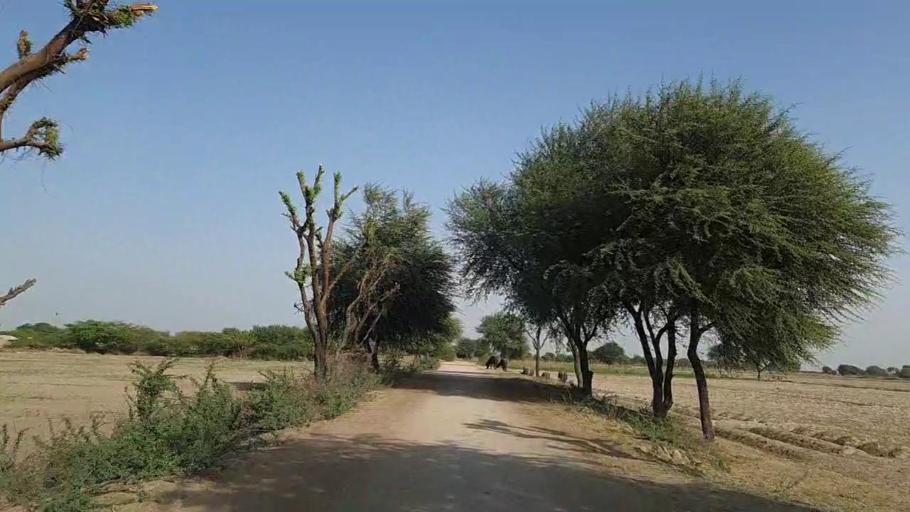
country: PK
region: Sindh
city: Dhoro Naro
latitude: 25.4168
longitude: 69.5236
